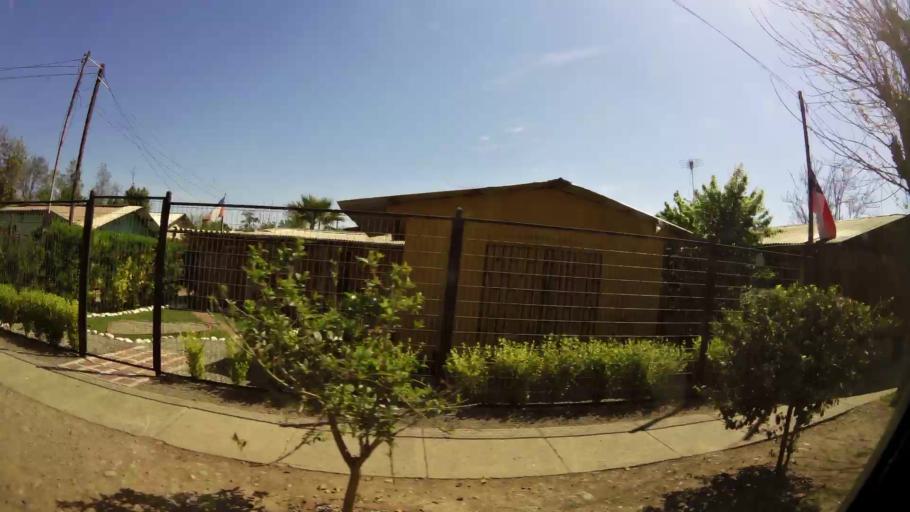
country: CL
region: Santiago Metropolitan
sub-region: Provincia de Talagante
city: Penaflor
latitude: -33.6079
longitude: -70.8837
